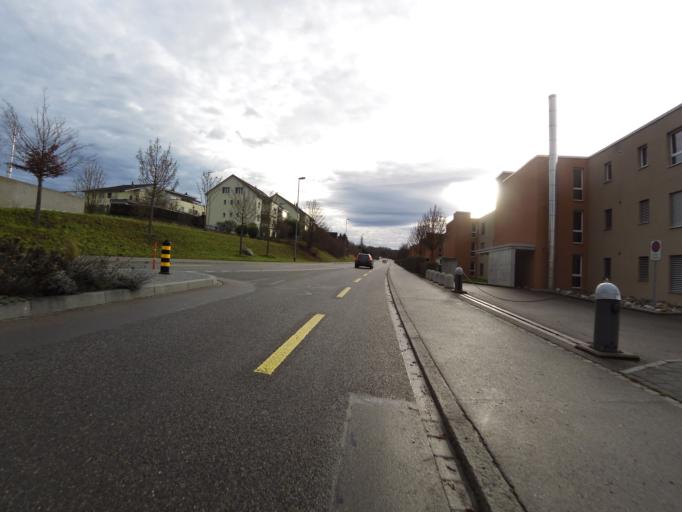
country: CH
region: Thurgau
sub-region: Frauenfeld District
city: Frauenfeld
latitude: 47.5471
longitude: 8.9103
